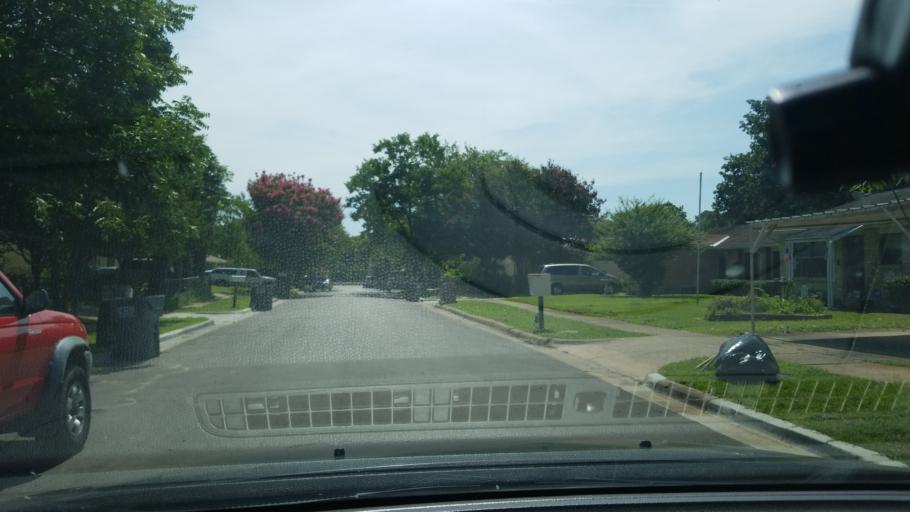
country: US
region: Texas
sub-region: Dallas County
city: Balch Springs
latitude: 32.7255
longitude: -96.6324
